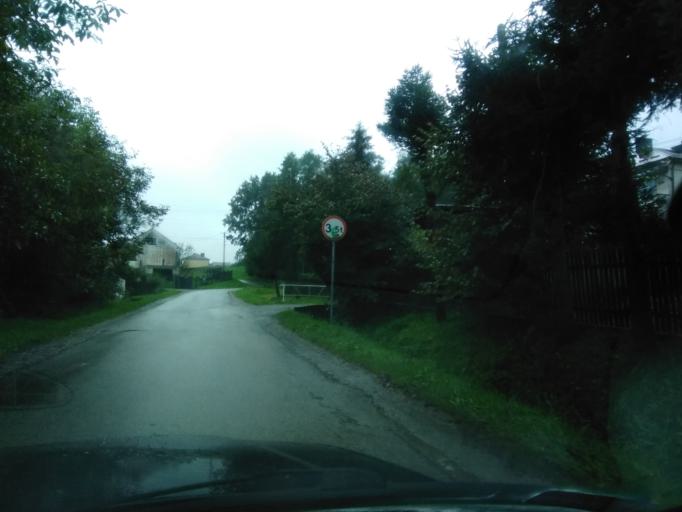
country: PL
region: Subcarpathian Voivodeship
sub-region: Powiat ropczycko-sedziszowski
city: Niedzwiada
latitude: 50.0255
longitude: 21.5411
